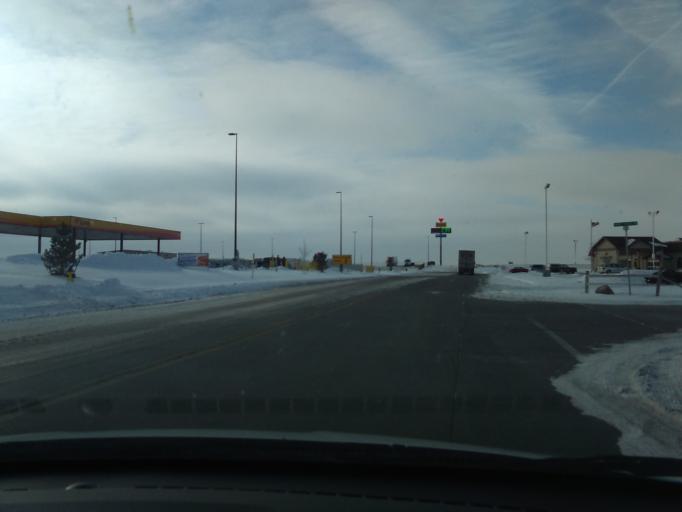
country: US
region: Nebraska
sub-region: Cheyenne County
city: Sidney
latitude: 41.1102
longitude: -102.9496
